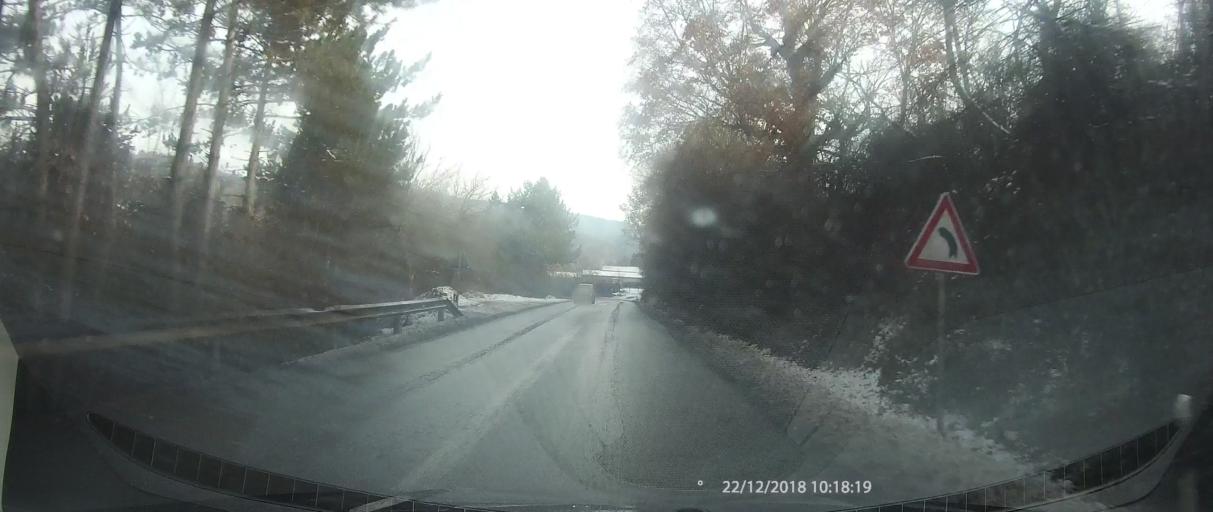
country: MK
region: Kriva Palanka
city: Kriva Palanka
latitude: 42.1864
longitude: 22.2815
